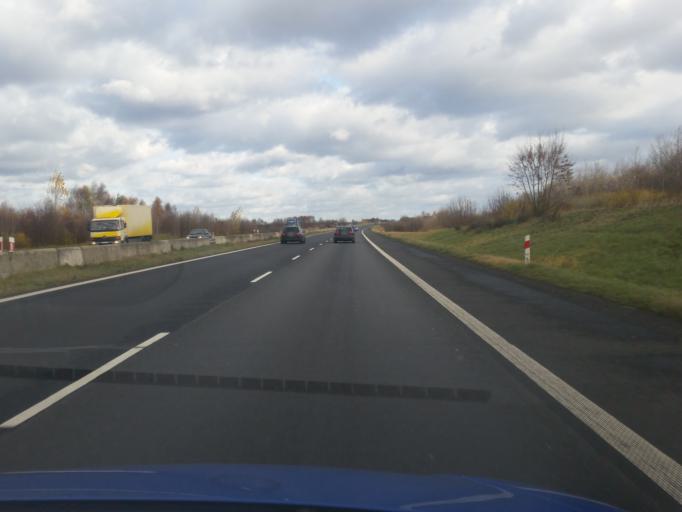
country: PL
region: Silesian Voivodeship
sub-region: Powiat czestochowski
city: Borowno
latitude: 50.9464
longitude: 19.2395
